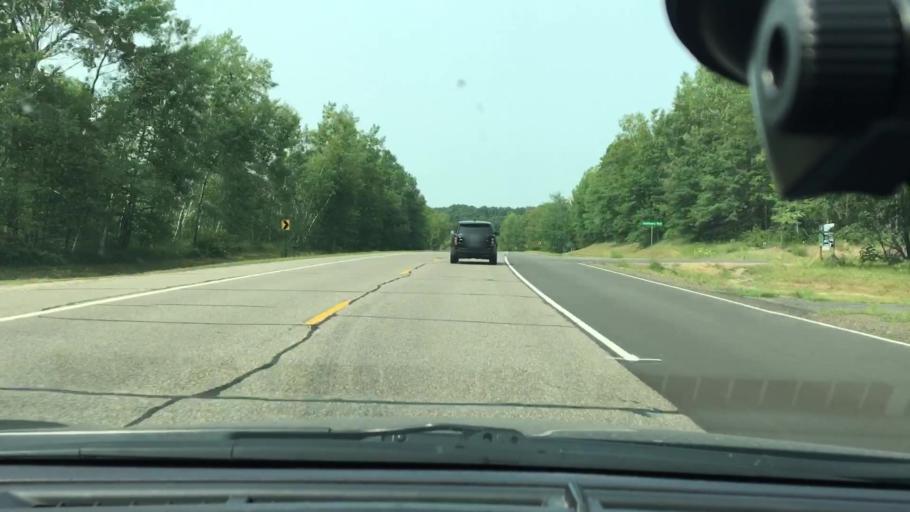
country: US
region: Minnesota
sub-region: Crow Wing County
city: Baxter
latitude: 46.3837
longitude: -94.3070
